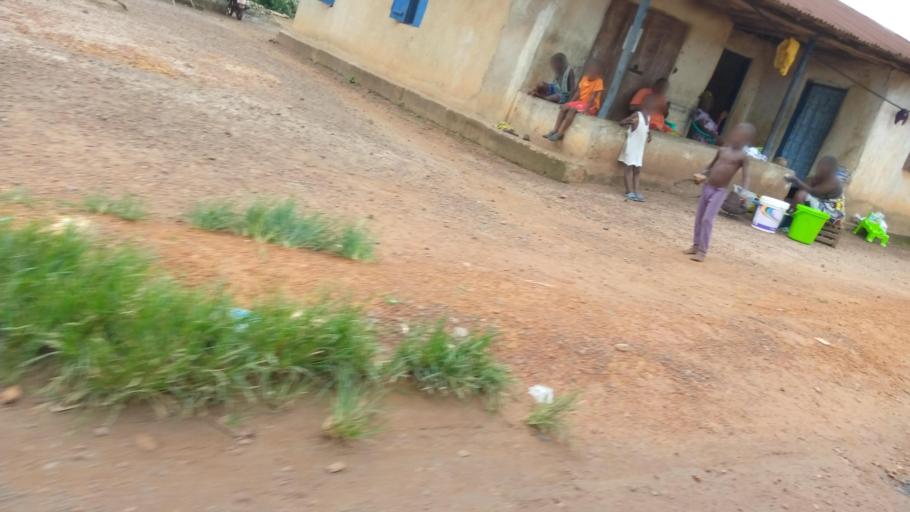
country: SL
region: Southern Province
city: Tongole
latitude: 7.4343
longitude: -11.8429
